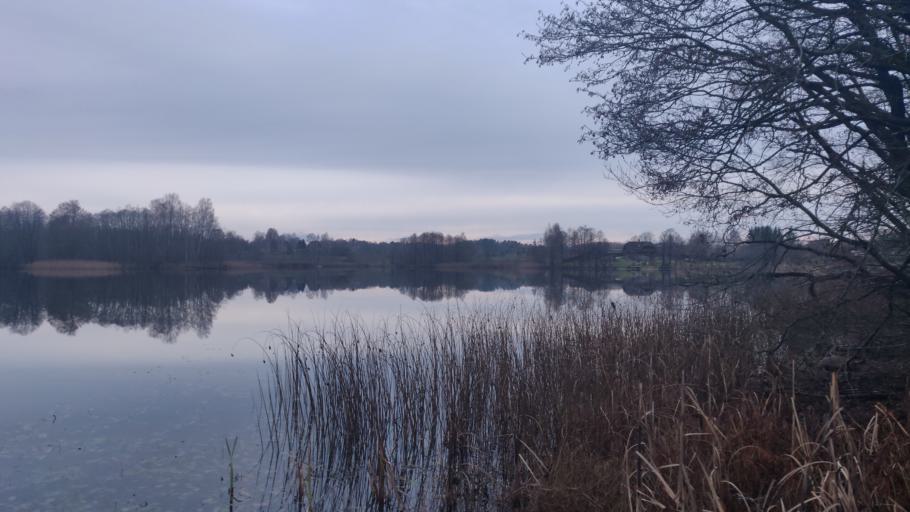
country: LT
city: Trakai
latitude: 54.6921
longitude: 24.9595
